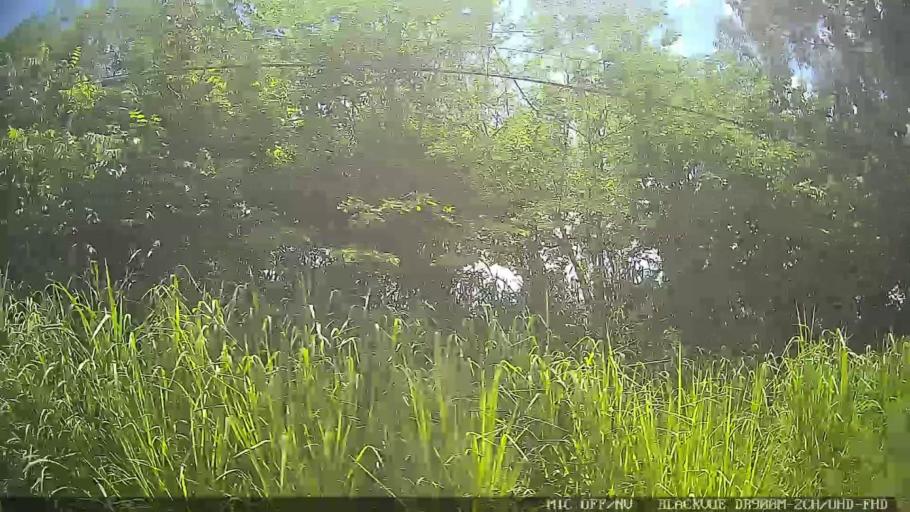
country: BR
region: Sao Paulo
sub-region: Laranjal Paulista
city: Laranjal Paulista
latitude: -23.0250
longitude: -47.8457
